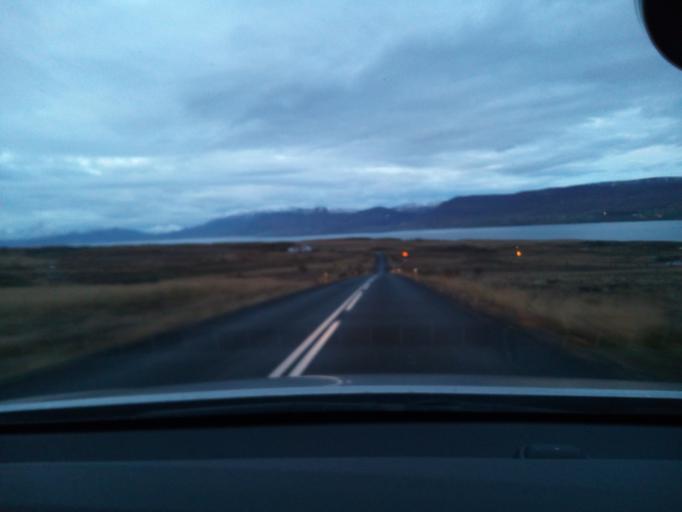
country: IS
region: Northeast
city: Akureyri
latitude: 65.7313
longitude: -18.1823
